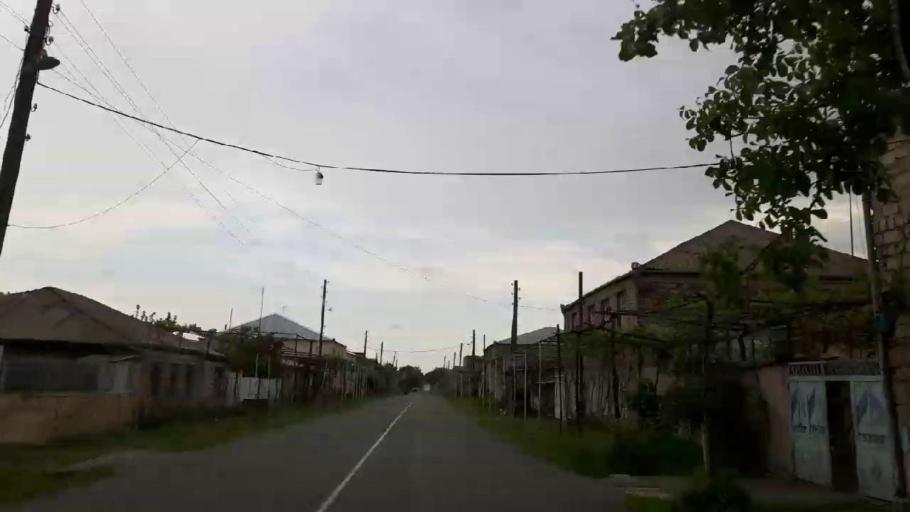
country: GE
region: Shida Kartli
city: Gori
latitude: 41.9618
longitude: 44.2027
